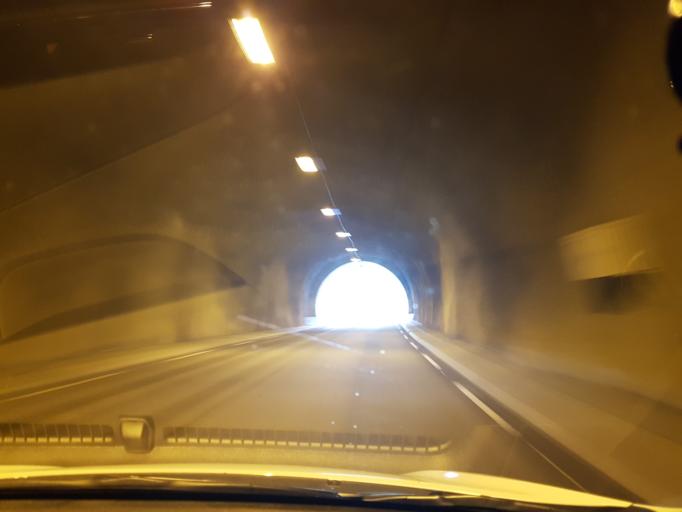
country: NO
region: Nord-Trondelag
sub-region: Stjordal
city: Stjordal
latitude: 63.6132
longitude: 10.9182
